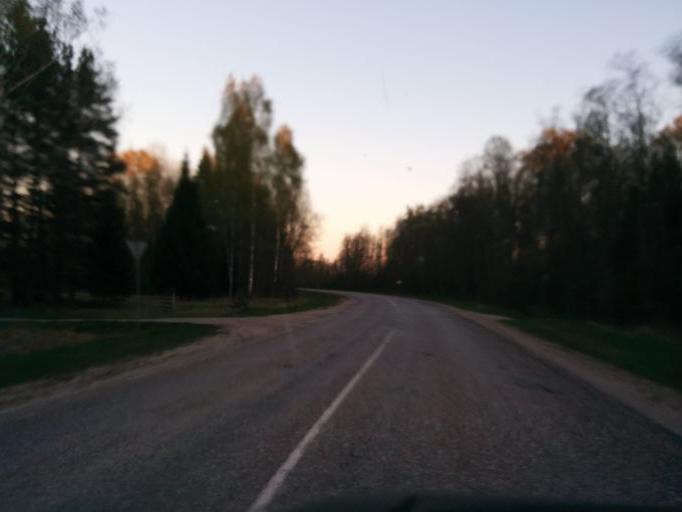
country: LV
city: Tireli
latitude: 56.8384
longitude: 23.5425
